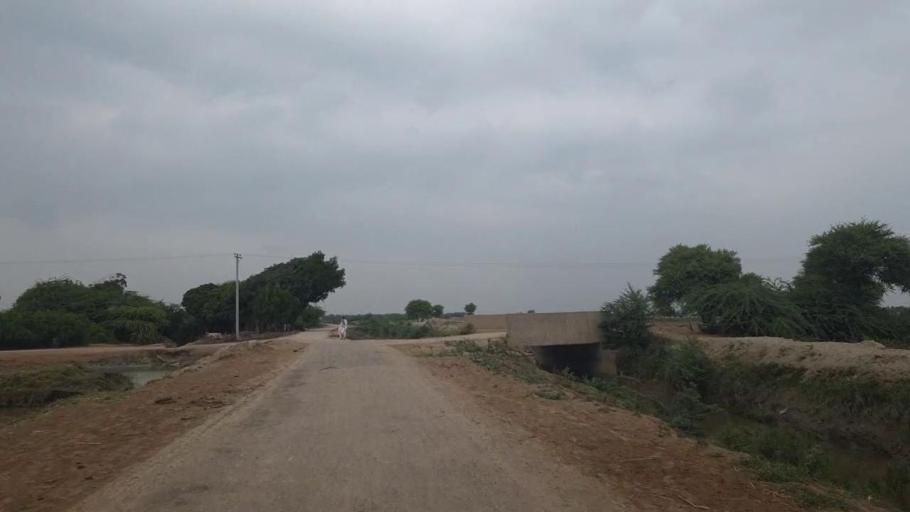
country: PK
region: Sindh
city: Badin
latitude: 24.6320
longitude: 68.6818
